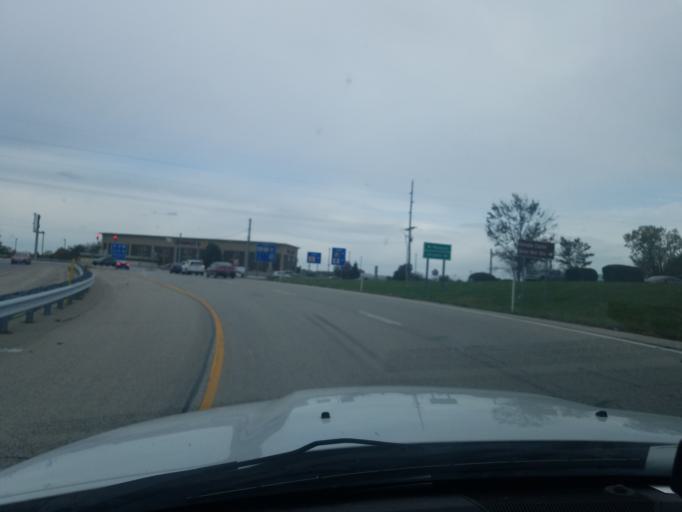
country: US
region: Indiana
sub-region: Harrison County
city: Corydon
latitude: 38.2379
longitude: -86.1280
